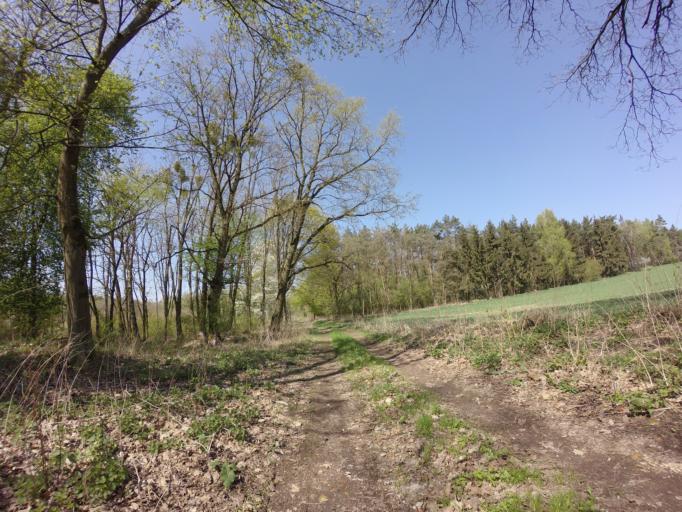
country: PL
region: West Pomeranian Voivodeship
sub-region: Powiat choszczenski
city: Choszczno
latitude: 53.1905
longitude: 15.3745
